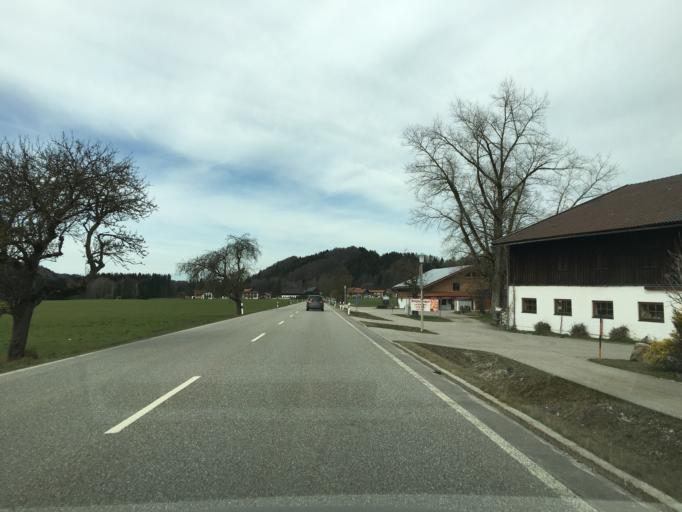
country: DE
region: Bavaria
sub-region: Upper Bavaria
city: Inzell
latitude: 47.7911
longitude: 12.7248
